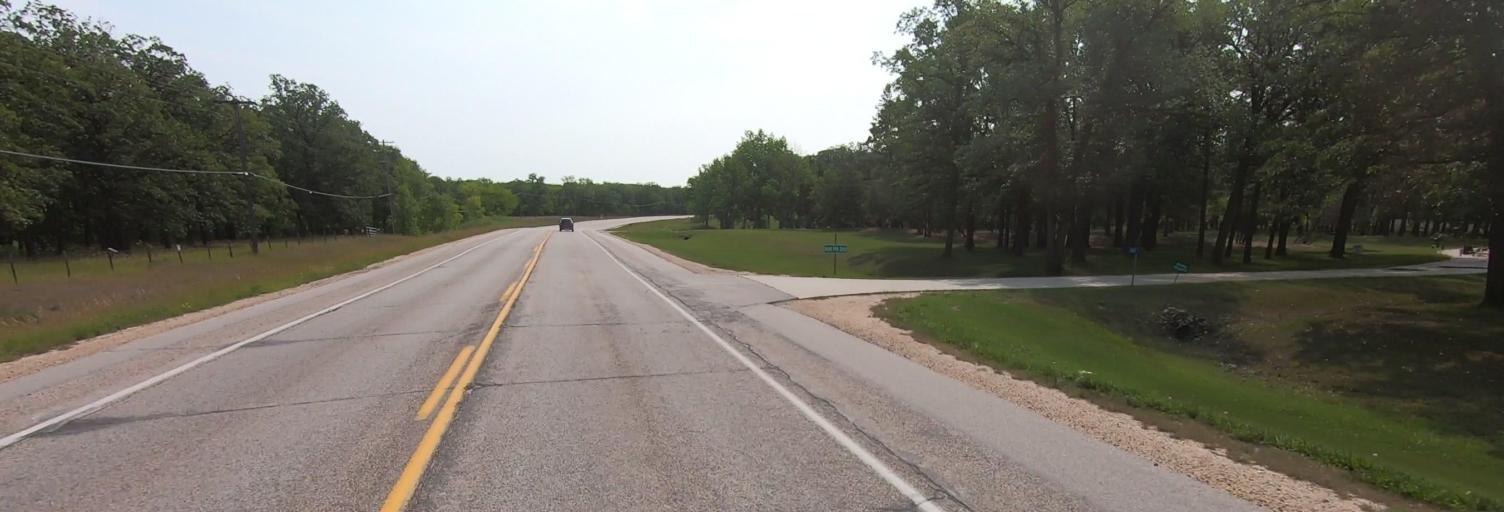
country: CA
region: Manitoba
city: Niverville
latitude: 49.7357
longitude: -97.1081
